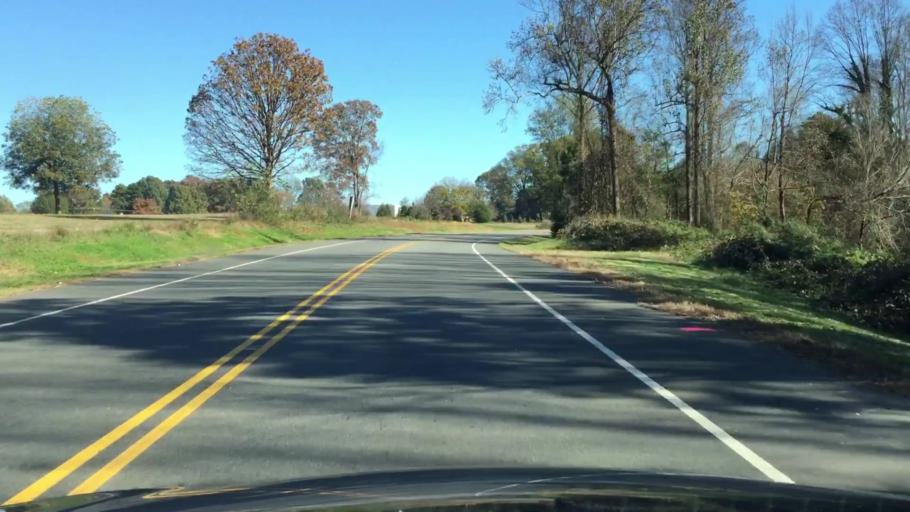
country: US
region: North Carolina
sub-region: Iredell County
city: Mooresville
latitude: 35.6141
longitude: -80.8256
